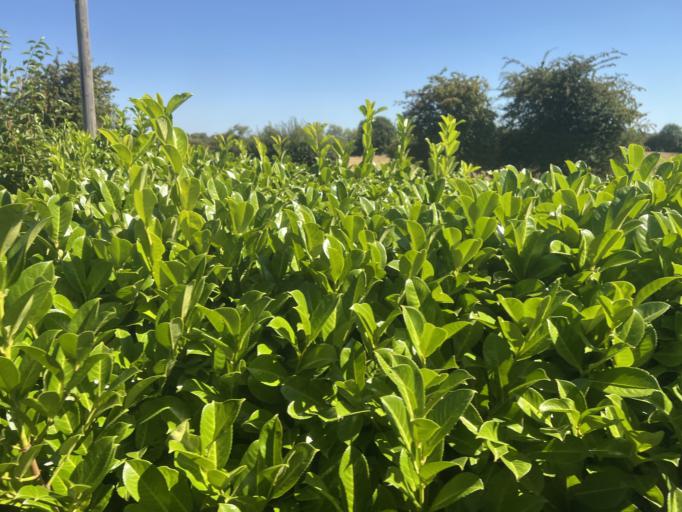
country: GB
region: England
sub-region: Lincolnshire
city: Wainfleet All Saints
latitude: 53.1233
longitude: 0.1992
